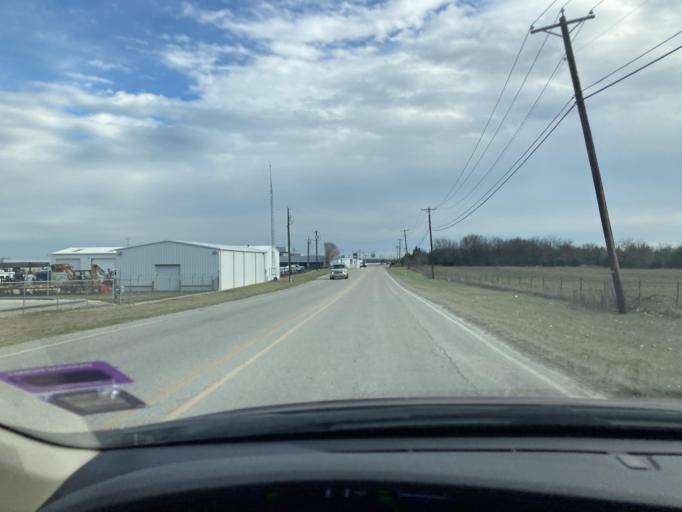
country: US
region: Texas
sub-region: Navarro County
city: Corsicana
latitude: 32.0610
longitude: -96.4551
